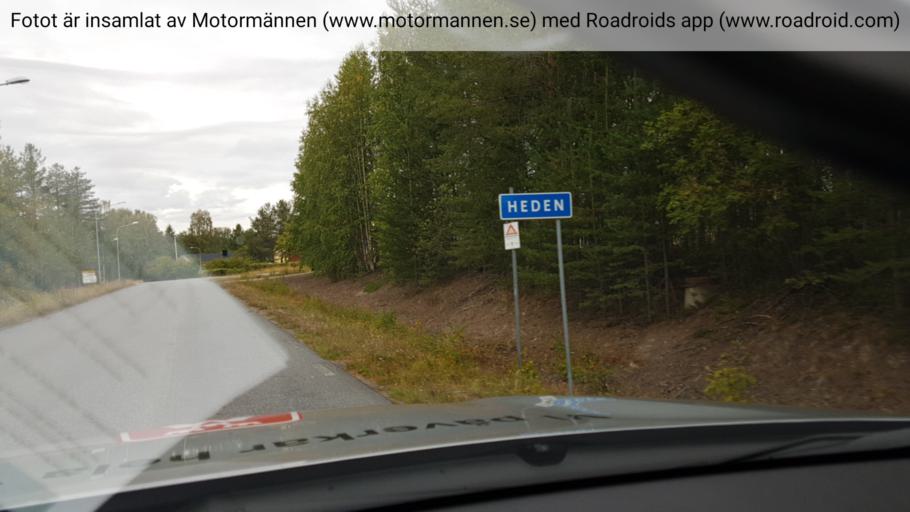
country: SE
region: Norrbotten
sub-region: Bodens Kommun
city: Boden
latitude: 65.8135
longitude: 21.5795
